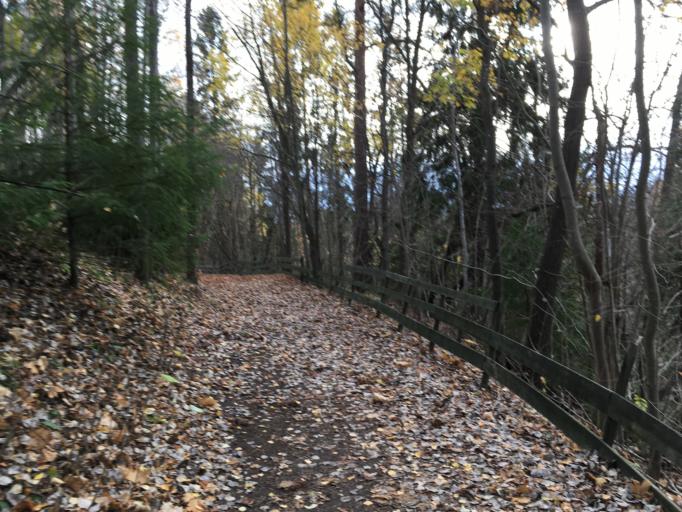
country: NO
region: Akershus
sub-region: Baerum
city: Lysaker
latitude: 59.9378
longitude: 10.6342
